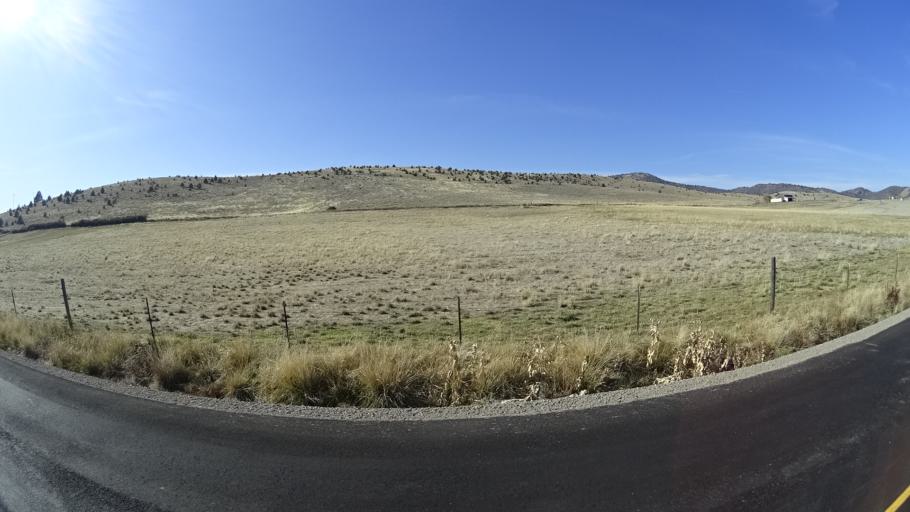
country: US
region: California
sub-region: Siskiyou County
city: Montague
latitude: 41.6049
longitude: -122.5301
